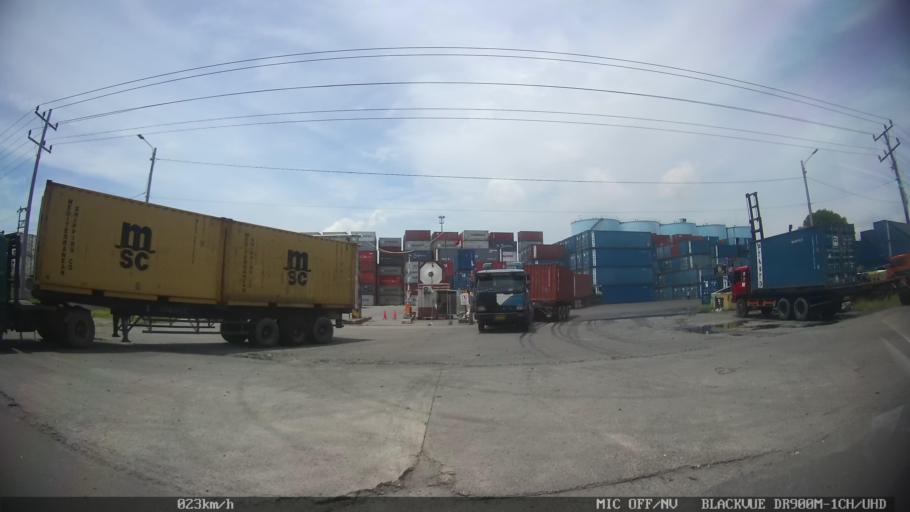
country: ID
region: North Sumatra
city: Belawan
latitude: 3.7787
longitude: 98.6984
